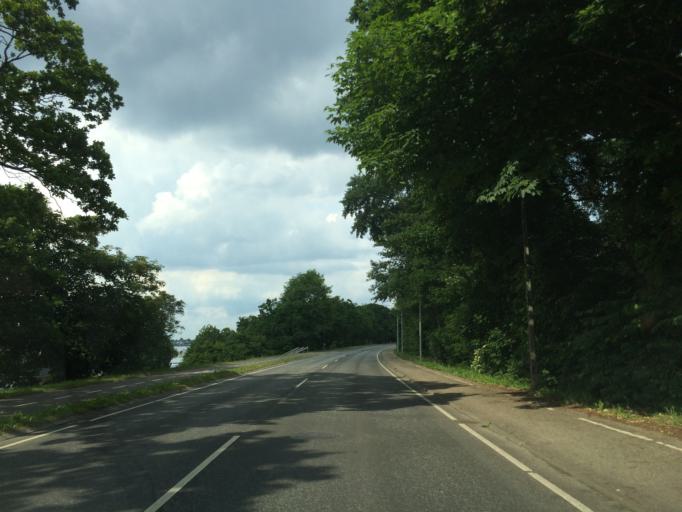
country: DK
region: South Denmark
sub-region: Middelfart Kommune
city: Strib
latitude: 55.5175
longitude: 9.7619
